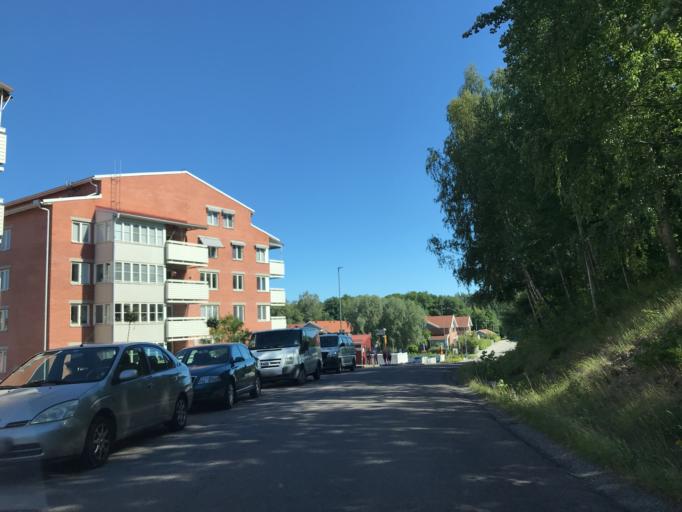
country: SE
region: Stockholm
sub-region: Upplands Vasby Kommun
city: Upplands Vaesby
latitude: 59.4824
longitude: 17.9255
